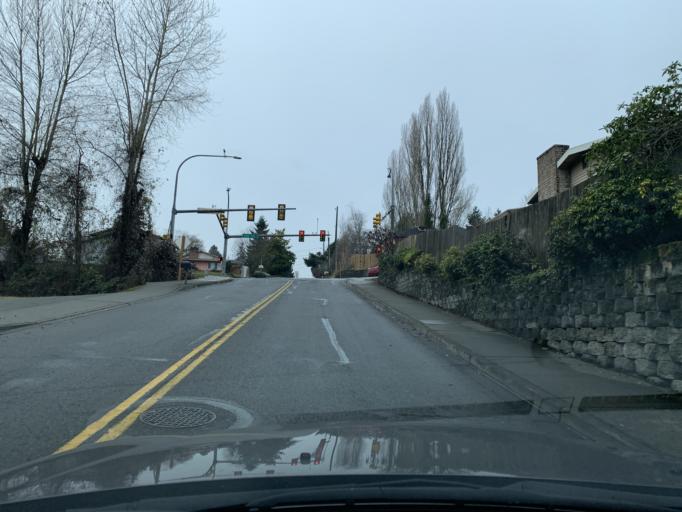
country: US
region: Washington
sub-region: King County
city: Tukwila
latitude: 47.4687
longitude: -122.2805
